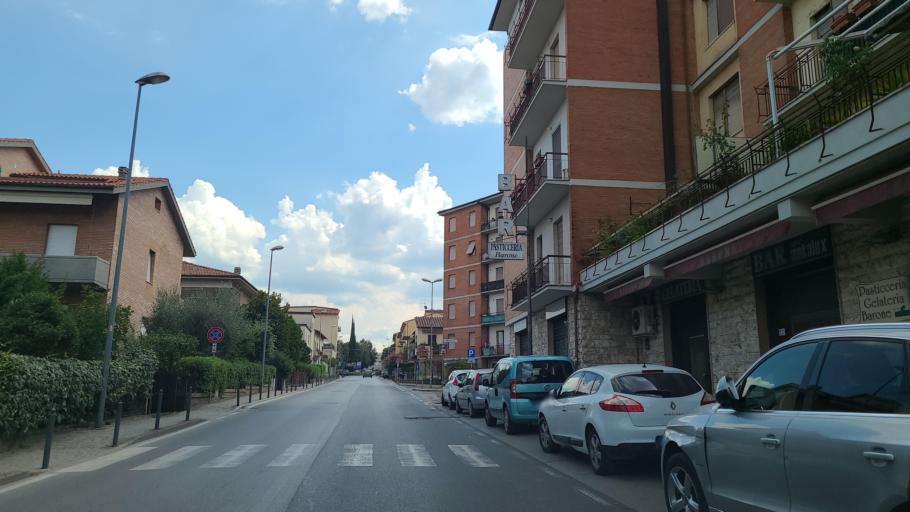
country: IT
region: Tuscany
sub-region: Provincia di Siena
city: Colle di Val d'Elsa
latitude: 43.4187
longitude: 11.1288
